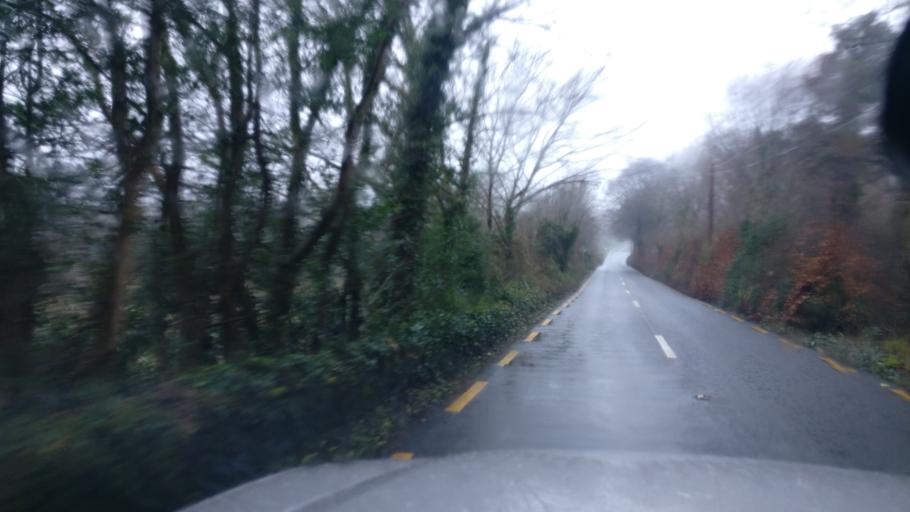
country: IE
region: Connaught
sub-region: County Galway
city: Loughrea
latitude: 53.1367
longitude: -8.4650
